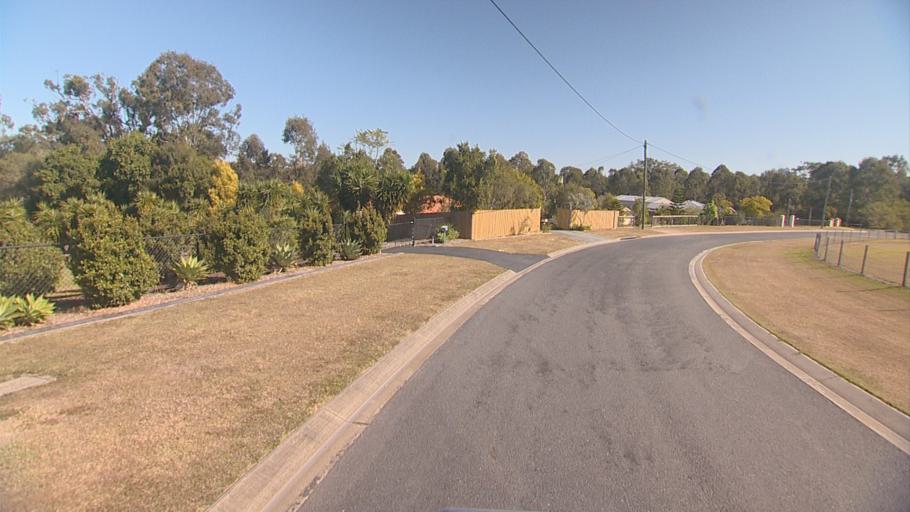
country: AU
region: Queensland
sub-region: Logan
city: Cedar Vale
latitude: -27.8568
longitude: 153.0107
